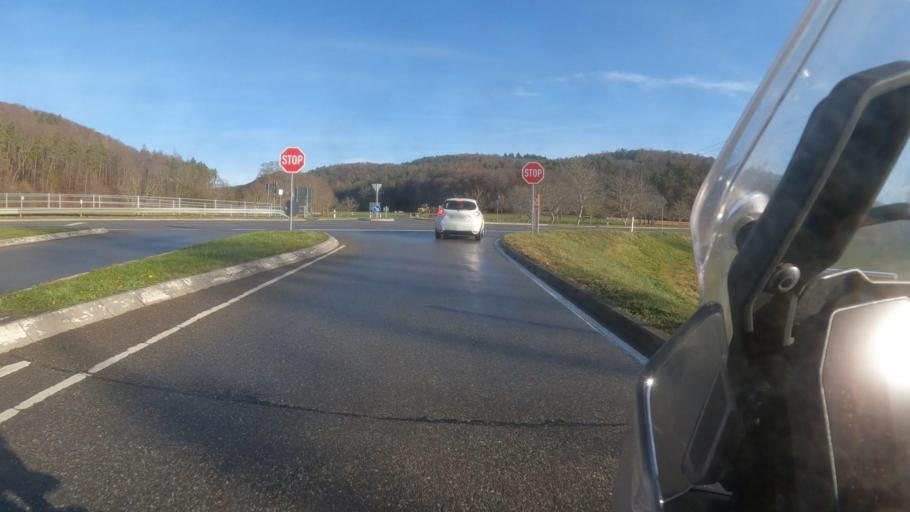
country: DE
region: Baden-Wuerttemberg
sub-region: Freiburg Region
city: Aach
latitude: 47.8504
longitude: 8.8290
